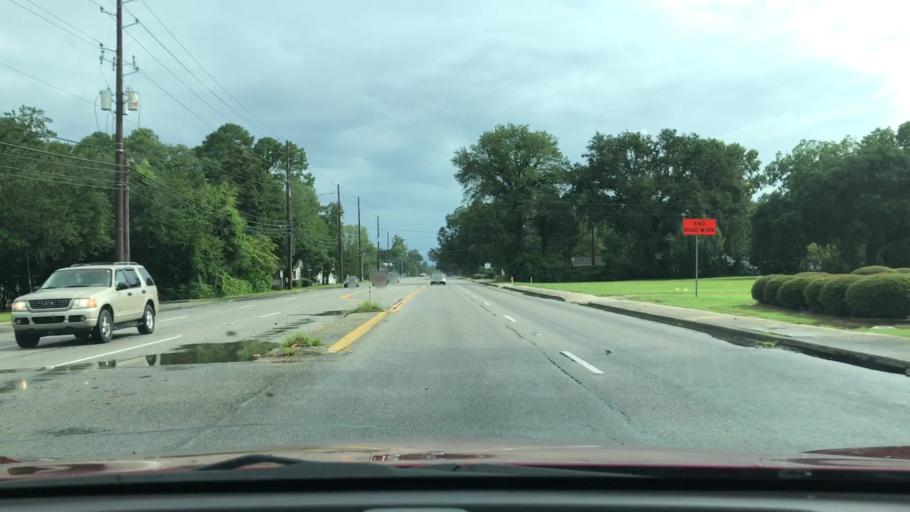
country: US
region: South Carolina
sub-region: Georgetown County
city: Georgetown
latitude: 33.4053
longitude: -79.2877
